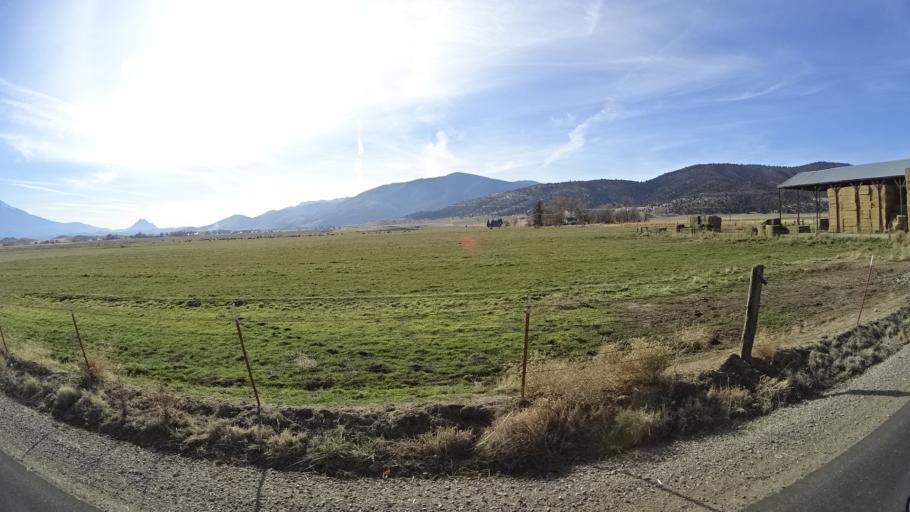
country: US
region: California
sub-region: Siskiyou County
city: Weed
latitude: 41.5380
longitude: -122.5342
